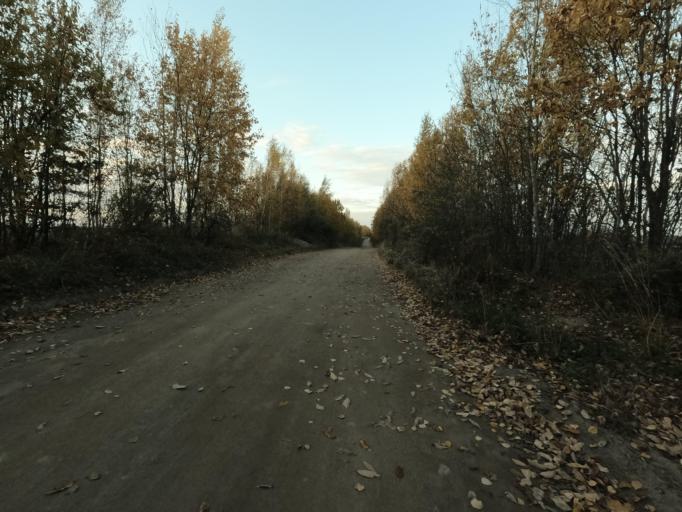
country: RU
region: Leningrad
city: Mga
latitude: 59.7900
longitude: 31.2016
